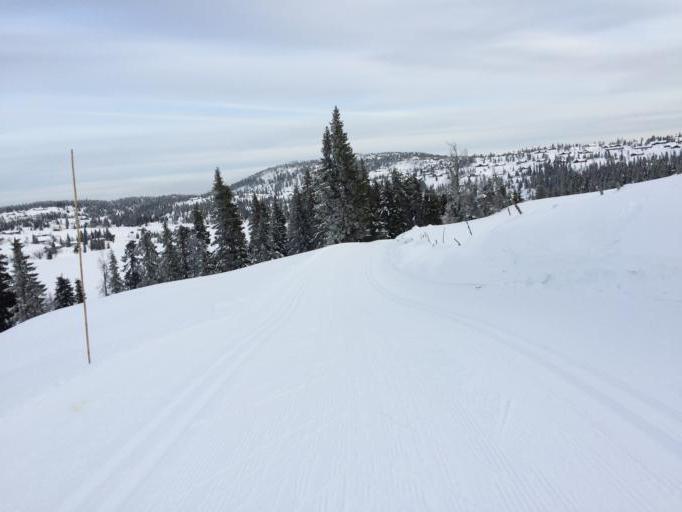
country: NO
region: Oppland
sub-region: Gausdal
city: Segalstad bru
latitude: 61.3125
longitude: 10.0553
